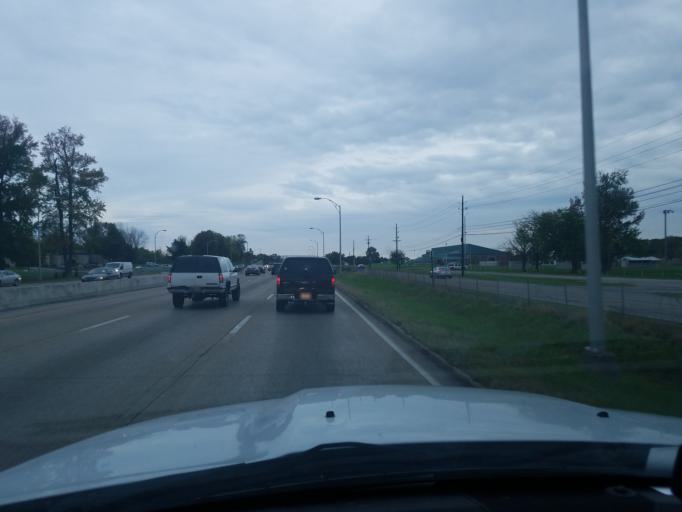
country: US
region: Indiana
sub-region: Vanderburgh County
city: Melody Hill
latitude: 37.9768
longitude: -87.5046
